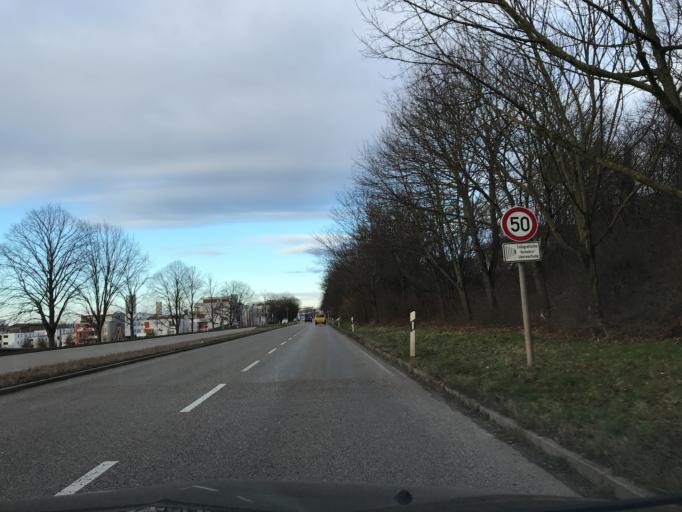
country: DE
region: Baden-Wuerttemberg
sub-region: Regierungsbezirk Stuttgart
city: Waiblingen
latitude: 48.8213
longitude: 9.3067
